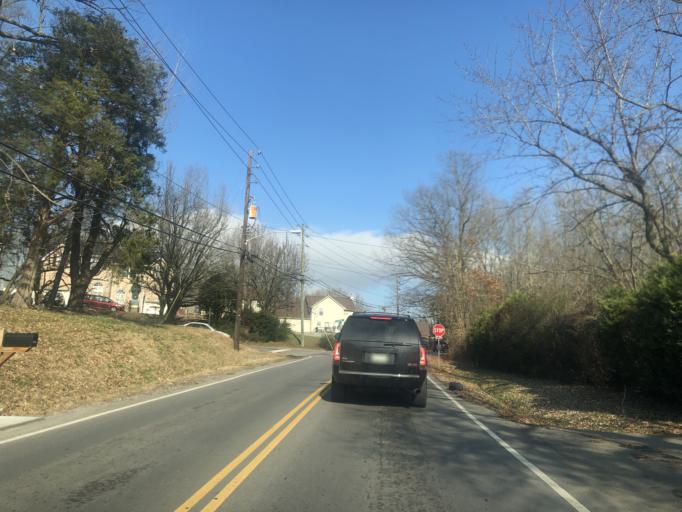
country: US
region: Tennessee
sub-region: Rutherford County
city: La Vergne
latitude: 36.0750
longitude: -86.6636
